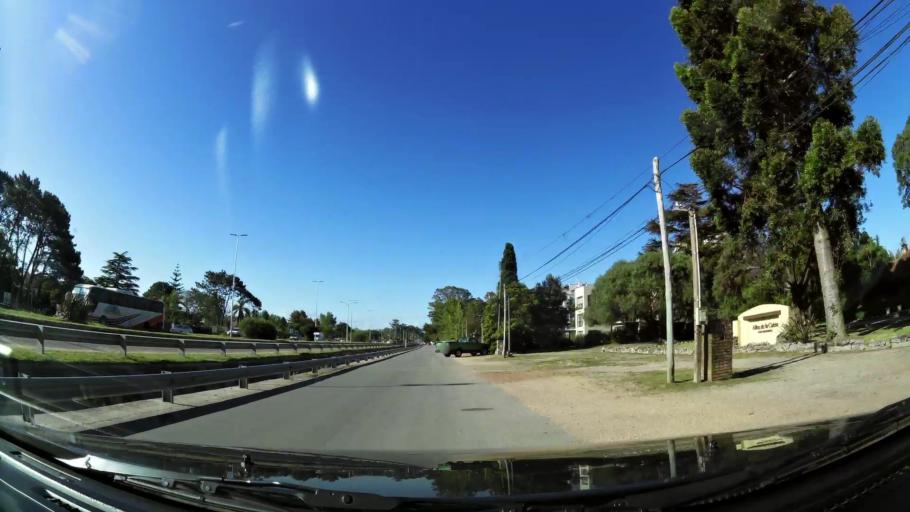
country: UY
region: Canelones
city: Barra de Carrasco
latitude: -34.8682
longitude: -56.0312
